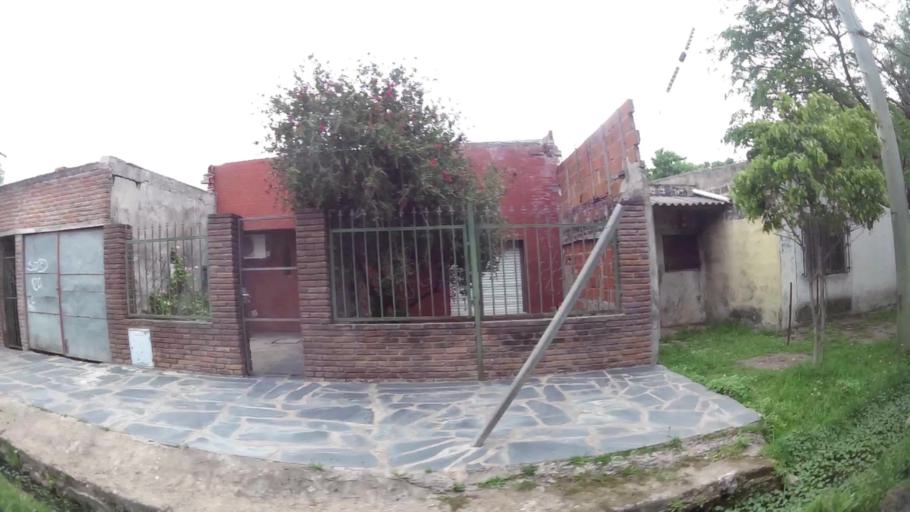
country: AR
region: Buenos Aires
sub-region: Partido de Campana
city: Campana
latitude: -34.2079
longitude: -58.9329
